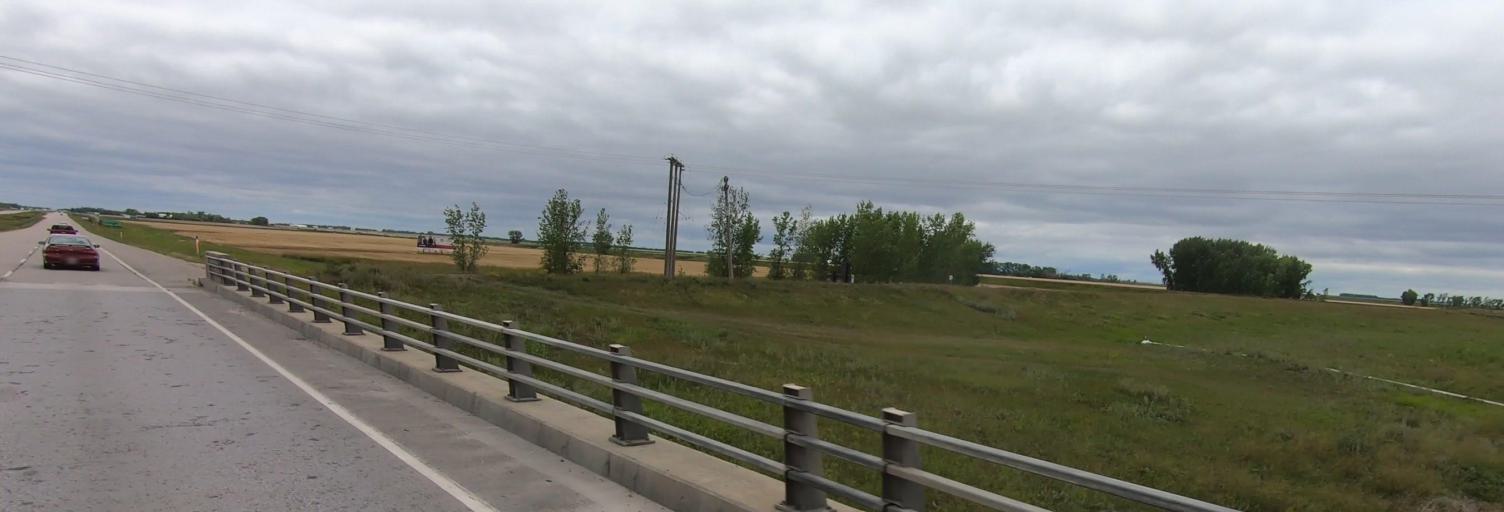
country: CA
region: Manitoba
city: Portage la Prairie
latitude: 49.9752
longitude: -98.3822
